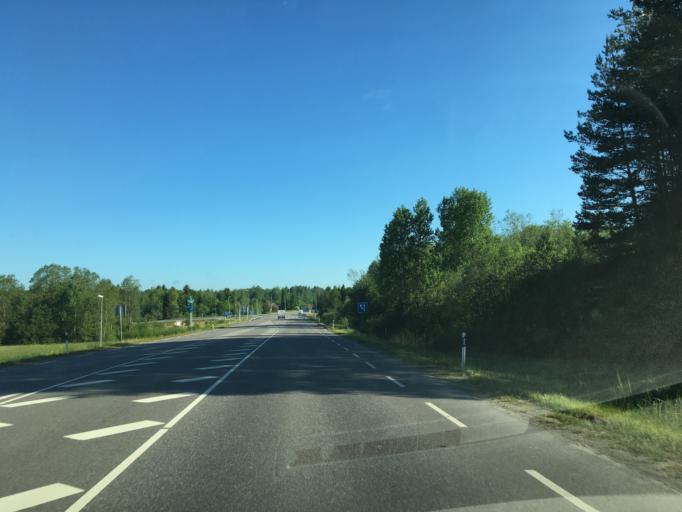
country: EE
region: Tartu
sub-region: Tartu linn
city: Tartu
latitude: 58.4566
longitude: 26.6731
